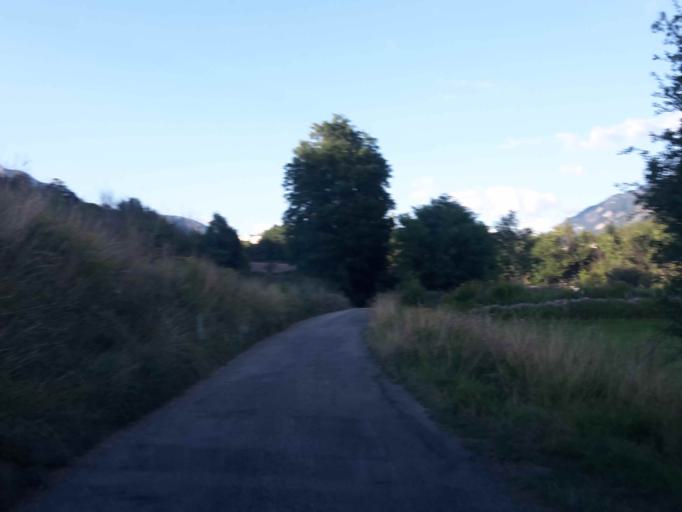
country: FR
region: Provence-Alpes-Cote d'Azur
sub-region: Departement des Hautes-Alpes
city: Embrun
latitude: 44.5629
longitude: 6.5039
